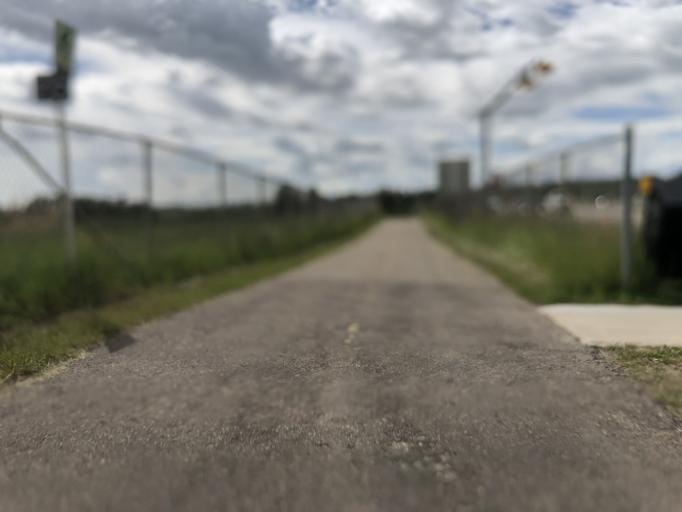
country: CA
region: Alberta
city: Calgary
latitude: 50.9824
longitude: -114.0351
